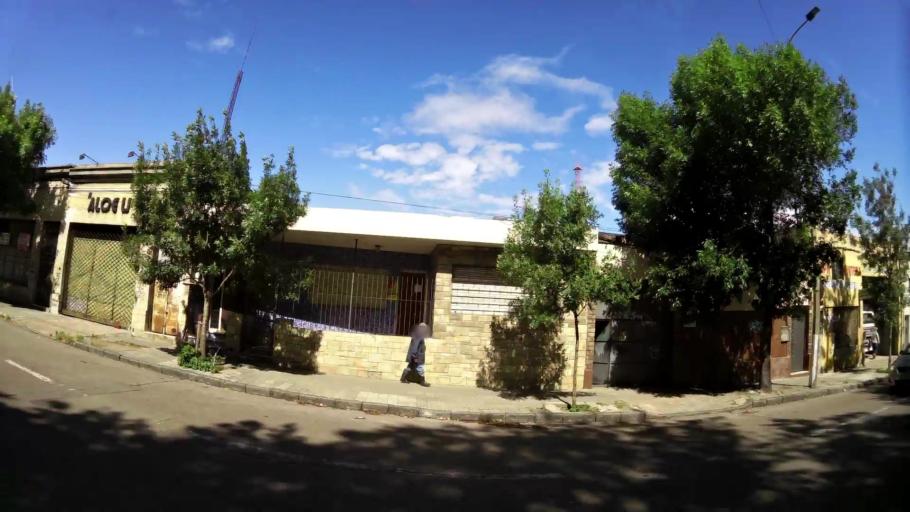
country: UY
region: Montevideo
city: Montevideo
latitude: -34.8801
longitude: -56.1876
